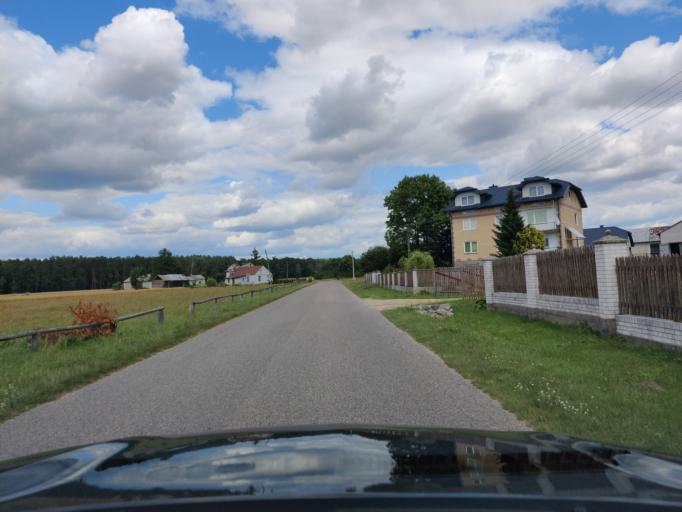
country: PL
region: Masovian Voivodeship
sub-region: Powiat wegrowski
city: Miedzna
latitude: 52.4876
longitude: 22.0243
